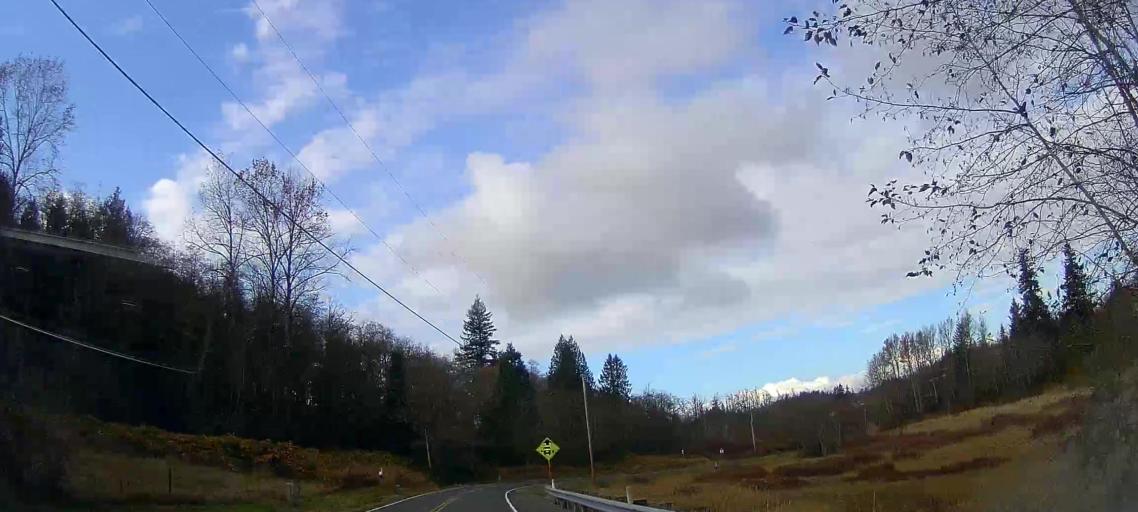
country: US
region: Washington
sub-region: Skagit County
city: Big Lake
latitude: 48.4073
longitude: -122.2169
